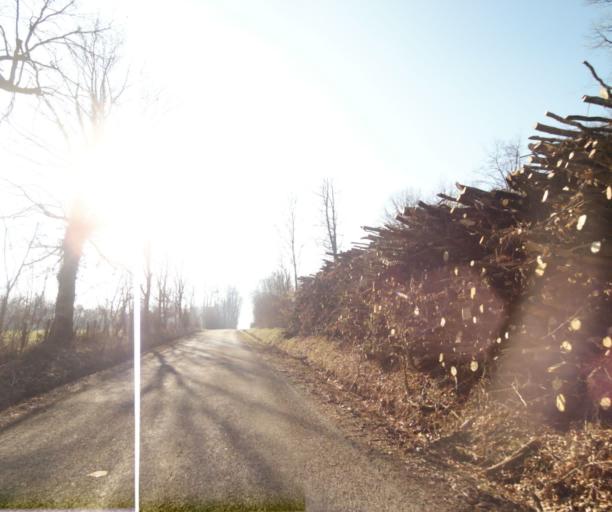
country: FR
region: Champagne-Ardenne
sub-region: Departement de la Haute-Marne
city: Wassy
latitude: 48.5093
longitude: 4.9642
